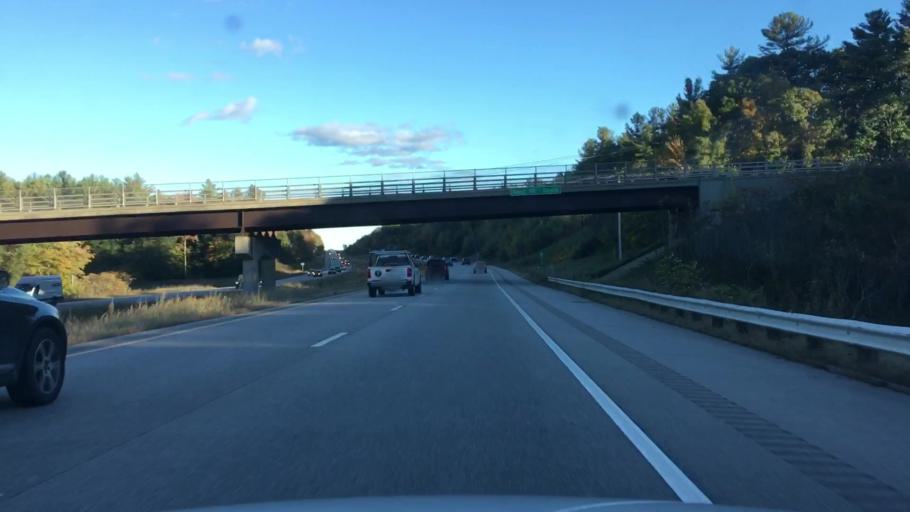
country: US
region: New Hampshire
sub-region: Rockingham County
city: Candia
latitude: 43.0344
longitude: -71.2558
